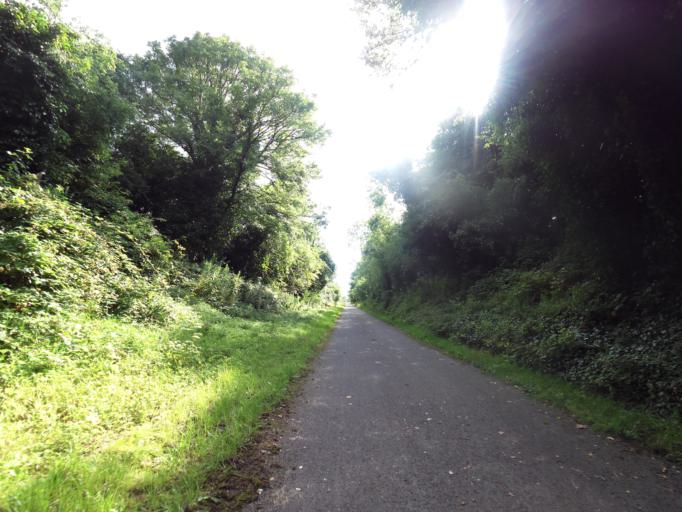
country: IE
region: Leinster
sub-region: An Iarmhi
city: Kilbeggan
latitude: 53.4845
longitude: -7.4658
